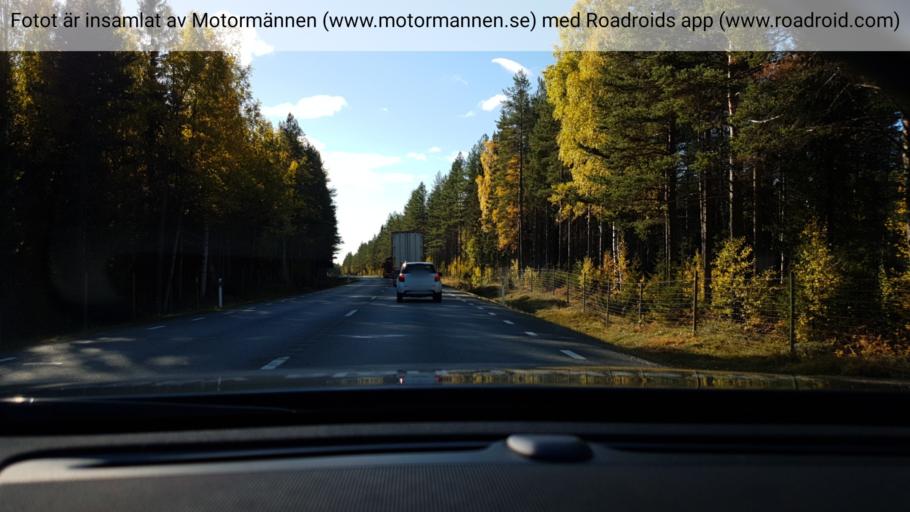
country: SE
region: Vaesterbotten
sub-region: Skelleftea Kommun
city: Burea
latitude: 64.5298
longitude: 21.2581
